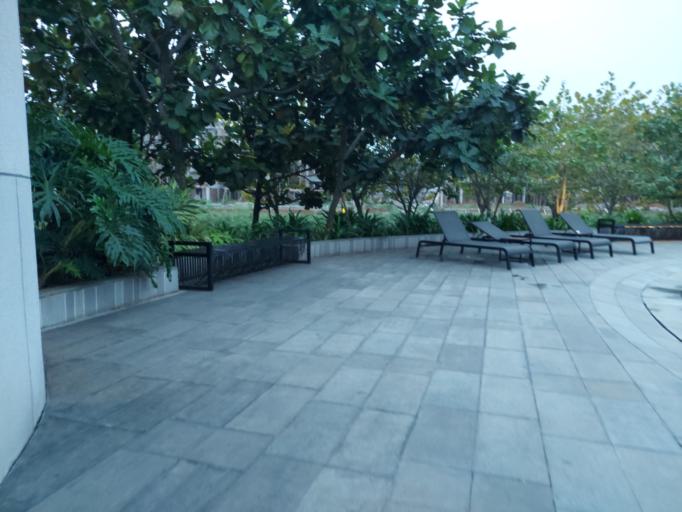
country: ID
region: West Java
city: Serpong
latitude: -6.2908
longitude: 106.6530
